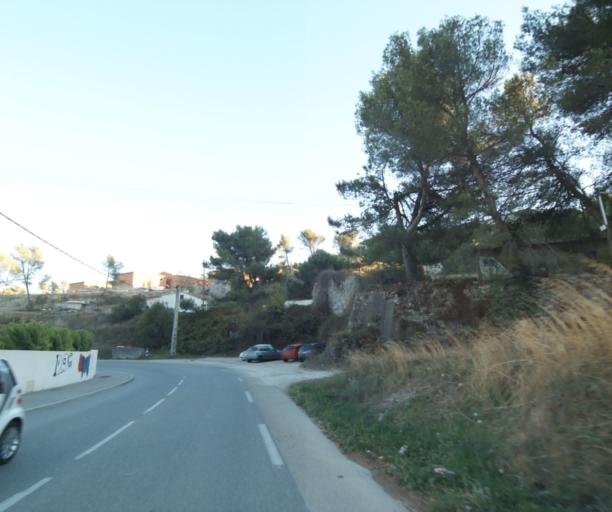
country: FR
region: Provence-Alpes-Cote d'Azur
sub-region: Departement des Bouches-du-Rhone
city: Carnoux-en-Provence
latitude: 43.2478
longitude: 5.5753
